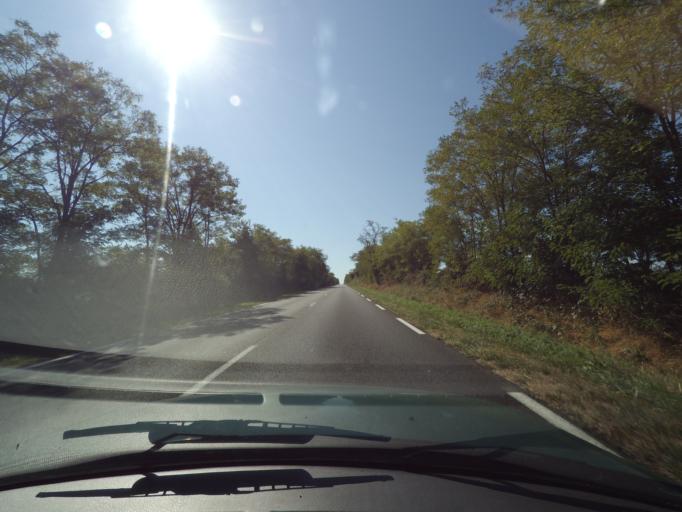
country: FR
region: Poitou-Charentes
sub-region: Departement de la Vienne
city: Saulge
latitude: 46.3417
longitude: 0.7984
